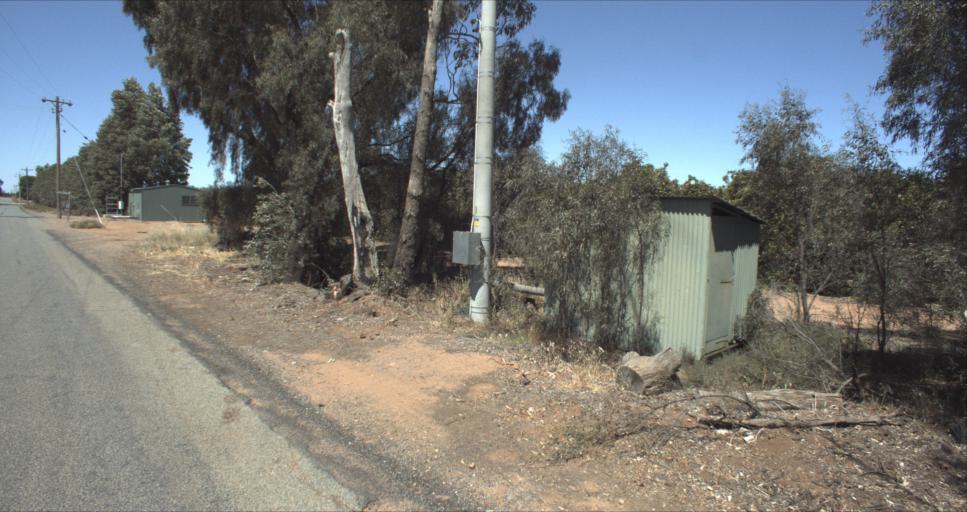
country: AU
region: New South Wales
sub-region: Leeton
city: Leeton
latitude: -34.5325
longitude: 146.3448
